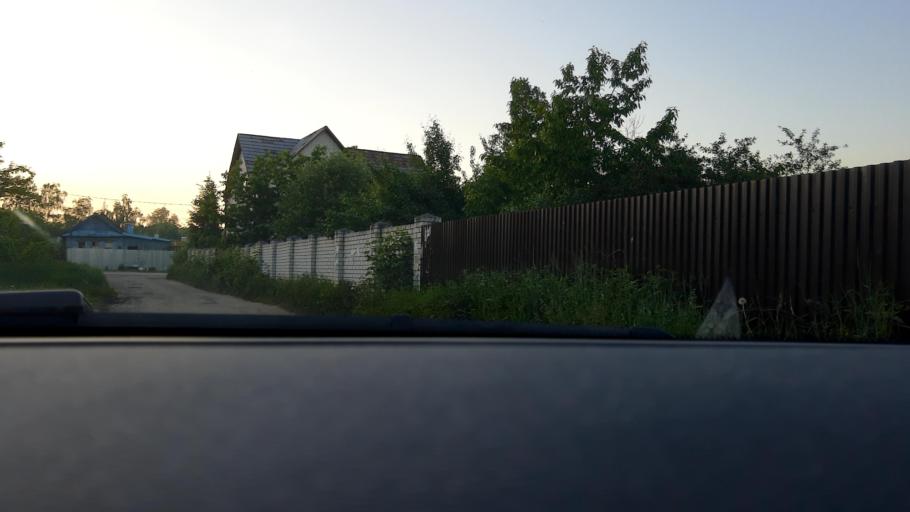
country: RU
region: Nizjnij Novgorod
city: Burevestnik
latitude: 56.2142
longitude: 43.8381
